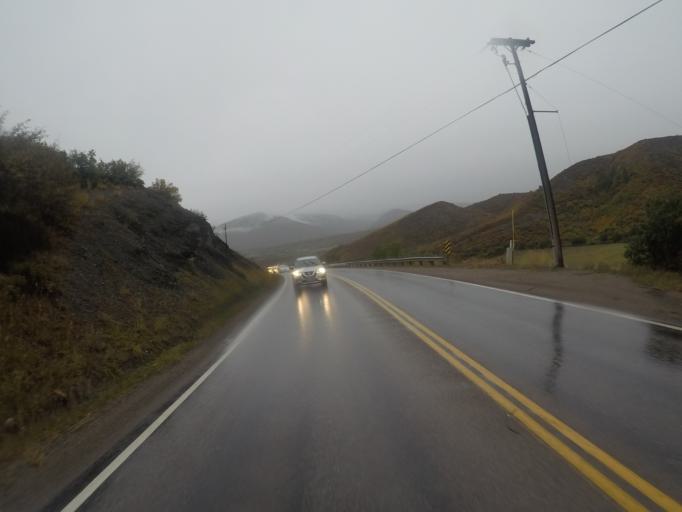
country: US
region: Colorado
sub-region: Pitkin County
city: Snowmass Village
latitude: 39.2413
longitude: -106.8937
